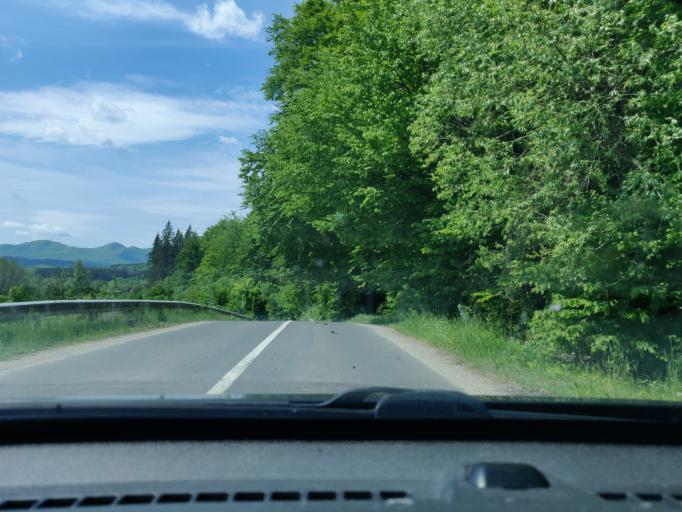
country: RO
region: Vrancea
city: Dragosloveni
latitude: 46.0356
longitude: 26.6983
